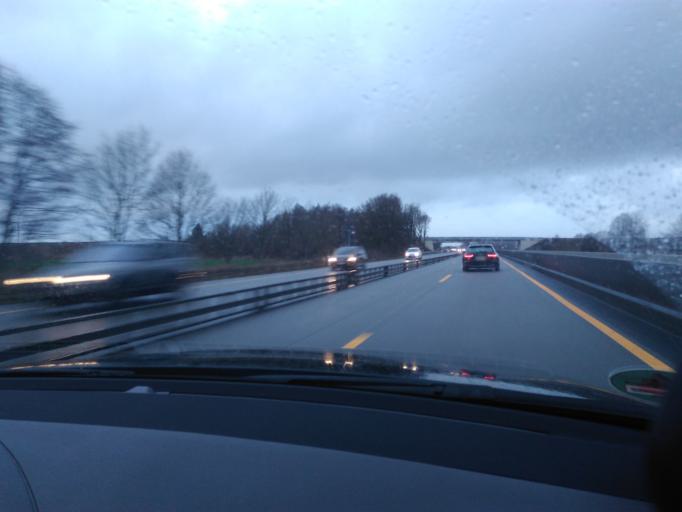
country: DE
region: Schleswig-Holstein
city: Grossenaspe
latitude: 53.9665
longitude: 9.9497
